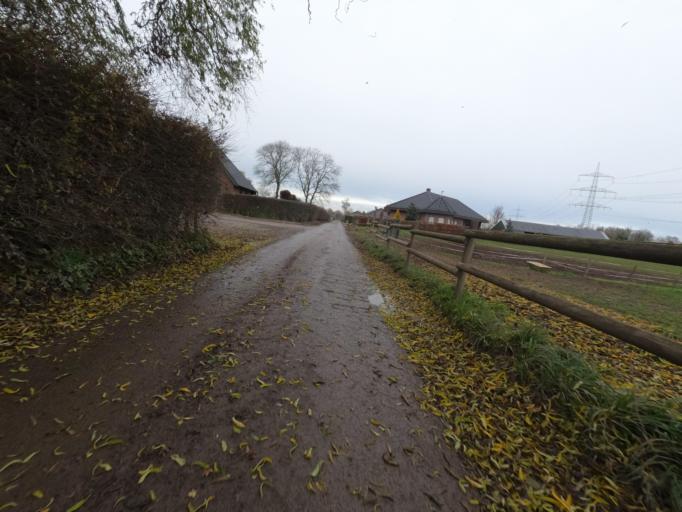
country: DE
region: North Rhine-Westphalia
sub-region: Regierungsbezirk Koln
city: Heinsberg
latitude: 51.0405
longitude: 6.1065
